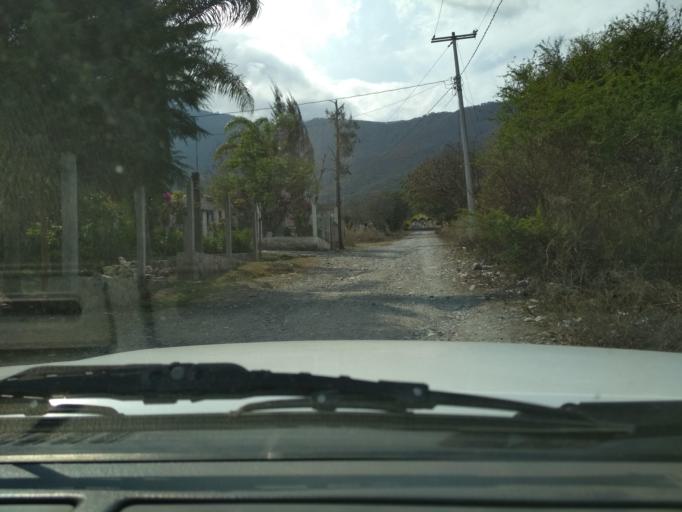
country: MX
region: Veracruz
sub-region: Acultzingo
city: Acatla
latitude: 18.7684
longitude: -97.2293
